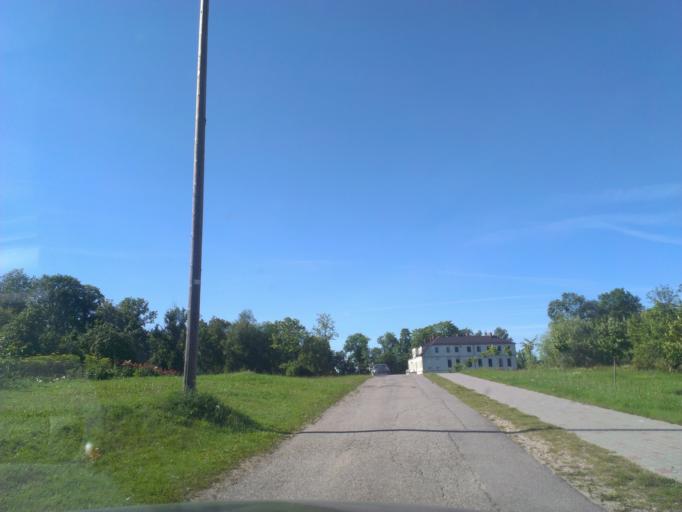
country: LV
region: Amatas Novads
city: Drabesi
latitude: 57.0672
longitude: 25.1883
